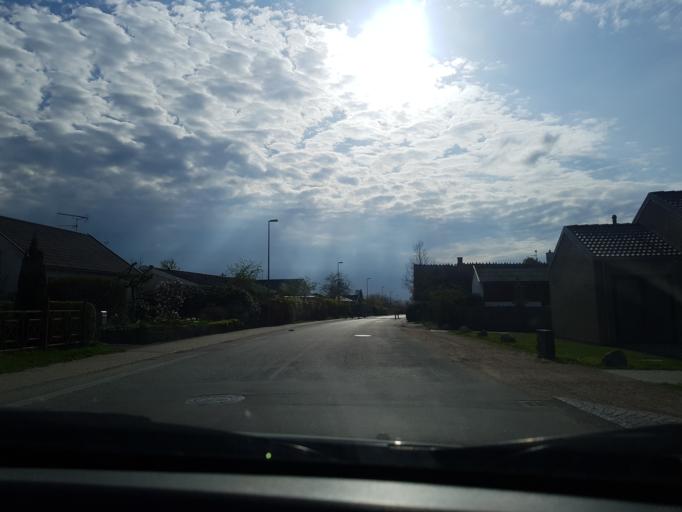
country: DK
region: Capital Region
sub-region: Allerod Kommune
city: Lillerod
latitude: 55.8590
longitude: 12.3347
